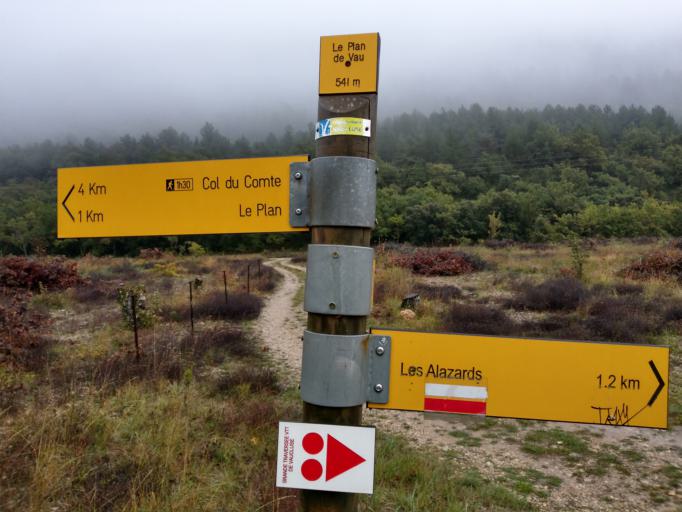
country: FR
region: Provence-Alpes-Cote d'Azur
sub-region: Departement du Vaucluse
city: Bedoin
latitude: 44.1867
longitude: 5.2118
